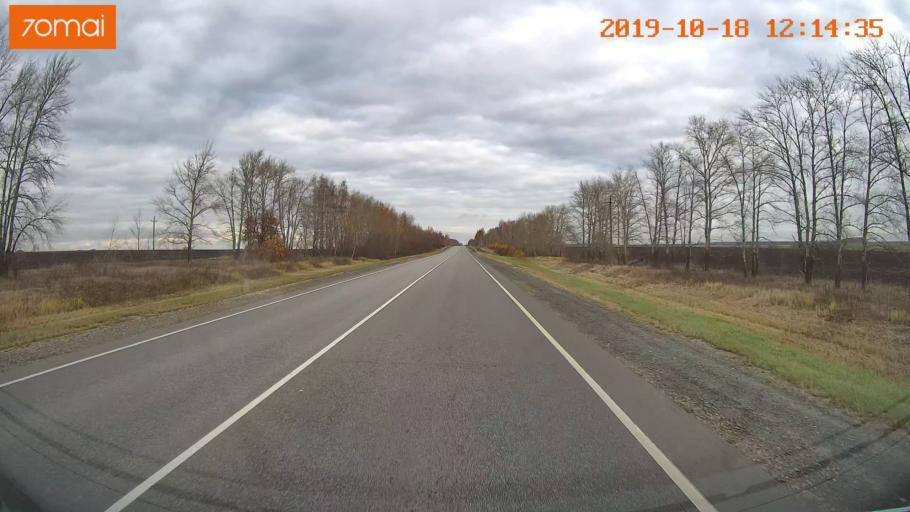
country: RU
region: Rjazan
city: Zakharovo
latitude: 54.4326
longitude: 39.3856
